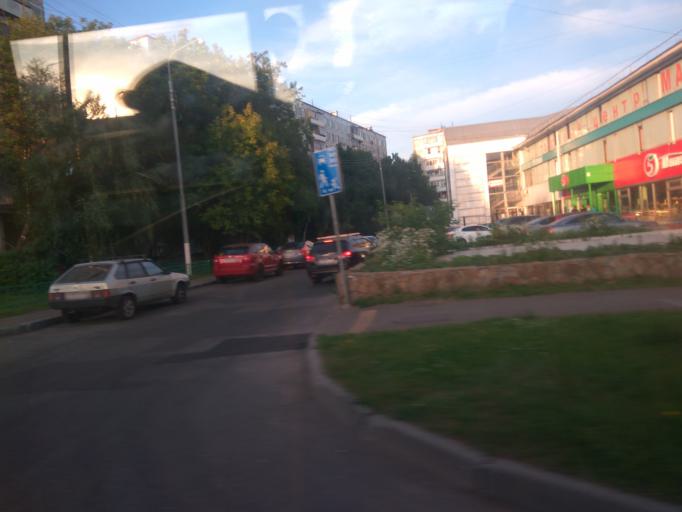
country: RU
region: Moscow
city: Chertanovo Yuzhnoye
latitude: 55.6087
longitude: 37.5790
